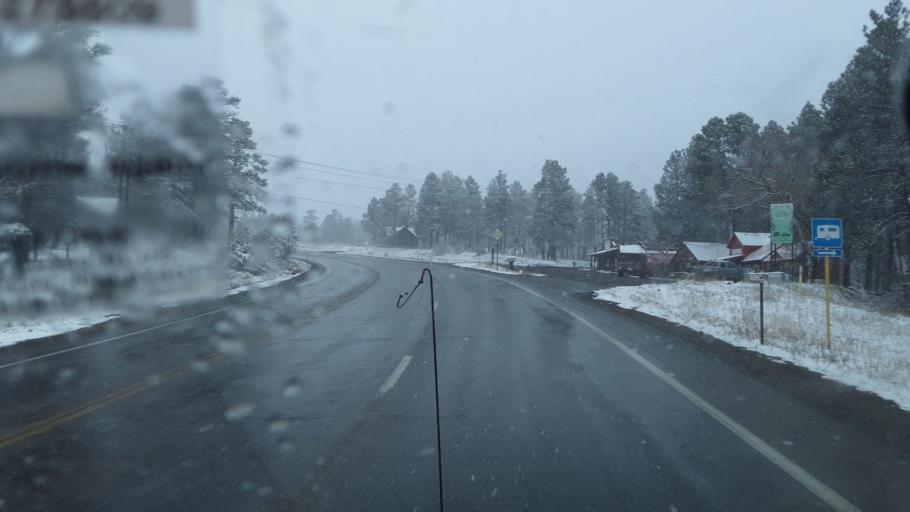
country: US
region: Colorado
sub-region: Archuleta County
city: Pagosa Springs
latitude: 37.2727
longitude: -107.0335
